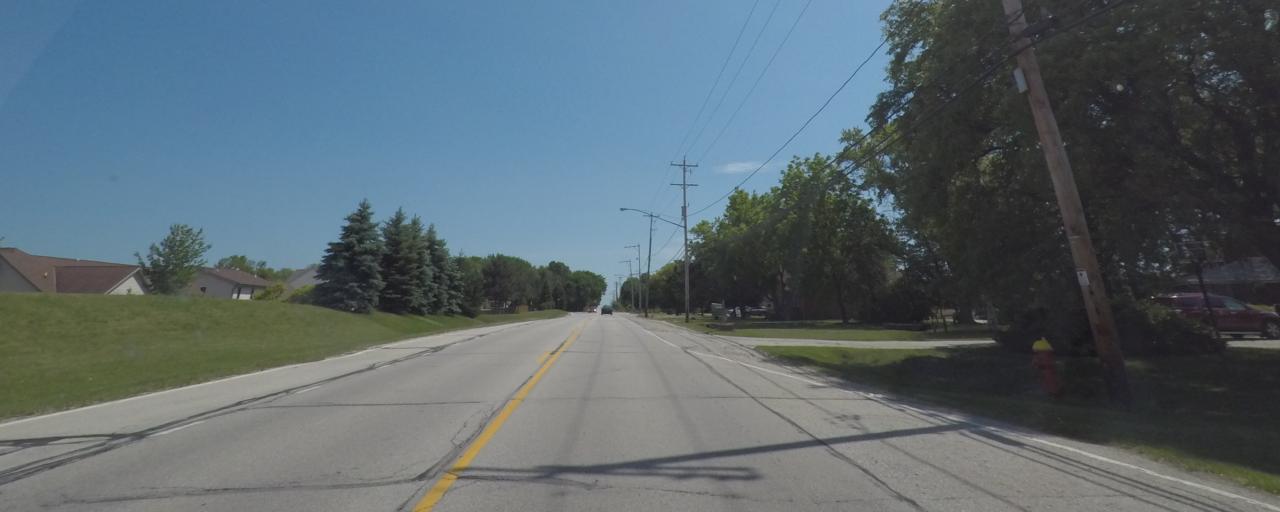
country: US
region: Wisconsin
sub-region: Milwaukee County
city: Oak Creek
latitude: 42.8840
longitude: -87.9319
